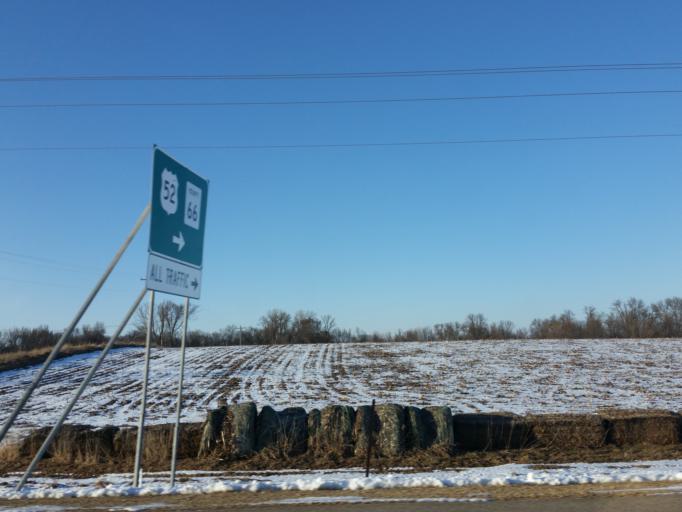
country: US
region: Minnesota
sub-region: Dakota County
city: Farmington
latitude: 44.6591
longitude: -93.0046
